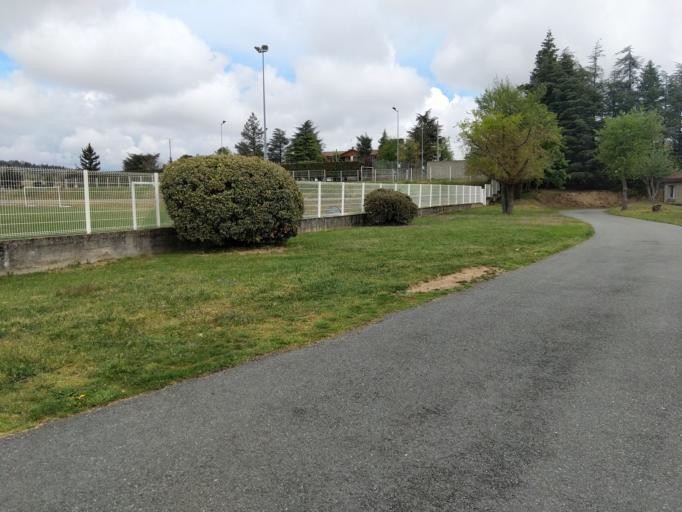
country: FR
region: Rhone-Alpes
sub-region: Departement de l'Ardeche
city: Roiffieux
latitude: 45.2222
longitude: 4.6510
